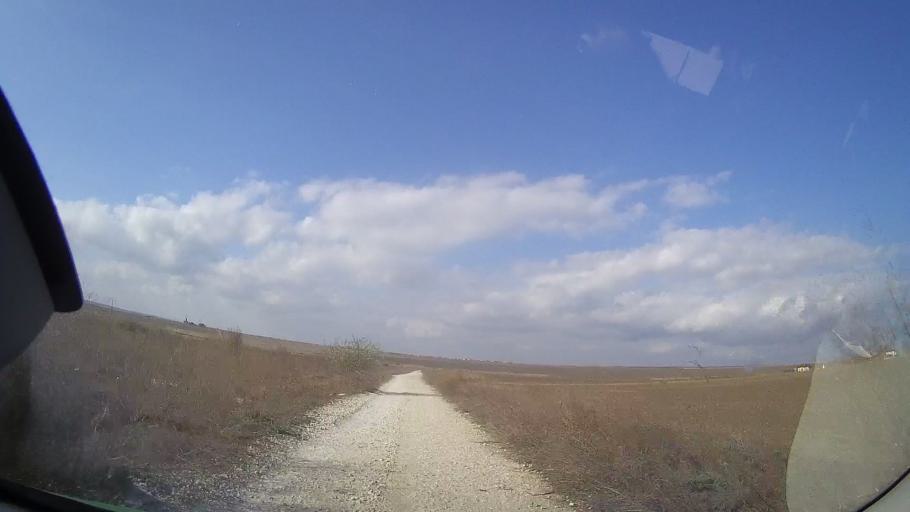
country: RO
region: Constanta
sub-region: Comuna Douazeci si Trei August
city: Douazeci si Trei August
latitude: 43.9062
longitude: 28.6139
